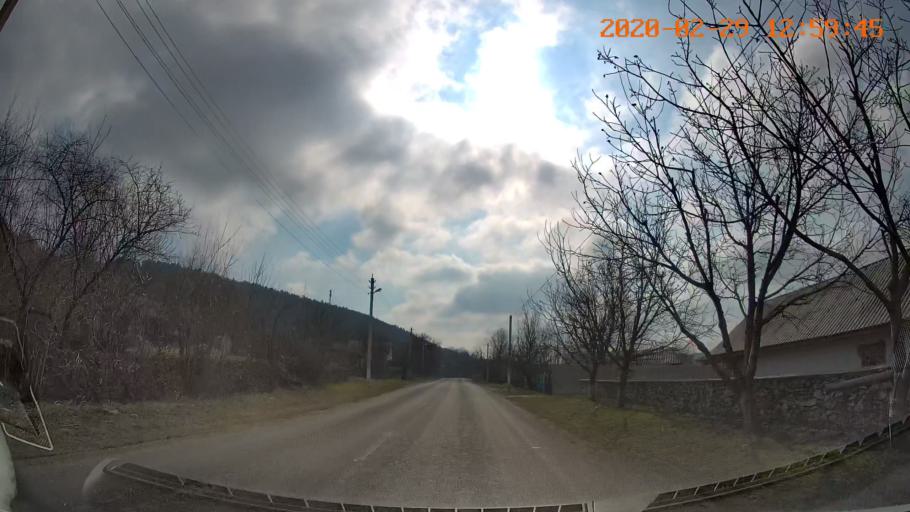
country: MD
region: Telenesti
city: Camenca
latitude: 48.0590
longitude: 28.7250
